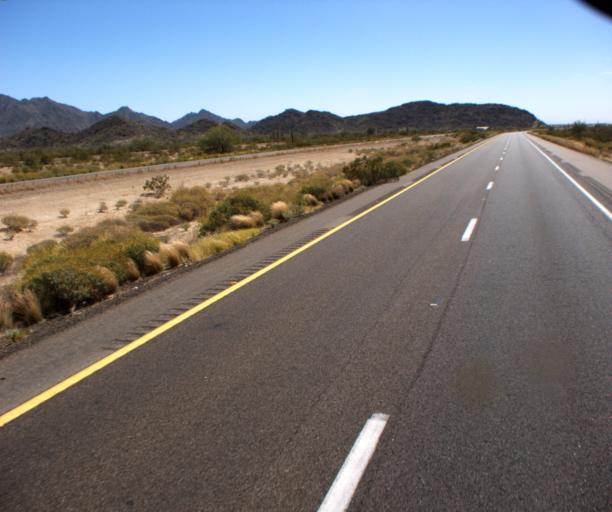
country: US
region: Arizona
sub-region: Maricopa County
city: Buckeye
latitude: 33.1856
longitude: -112.6517
